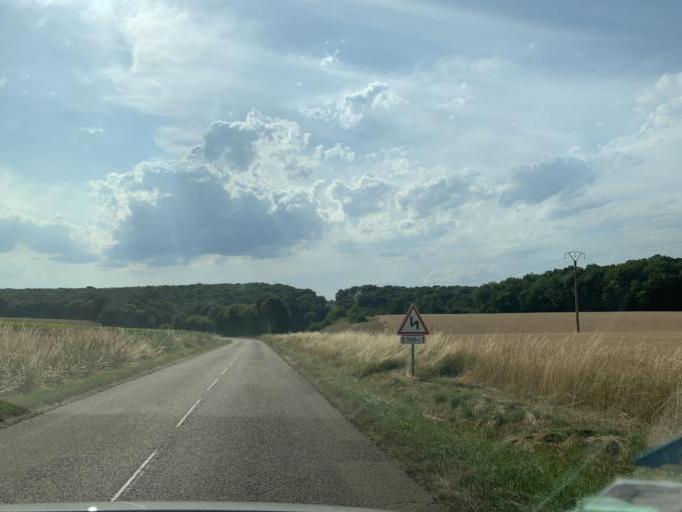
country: FR
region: Bourgogne
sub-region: Departement de l'Yonne
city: Fontenailles
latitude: 47.5187
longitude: 3.4153
